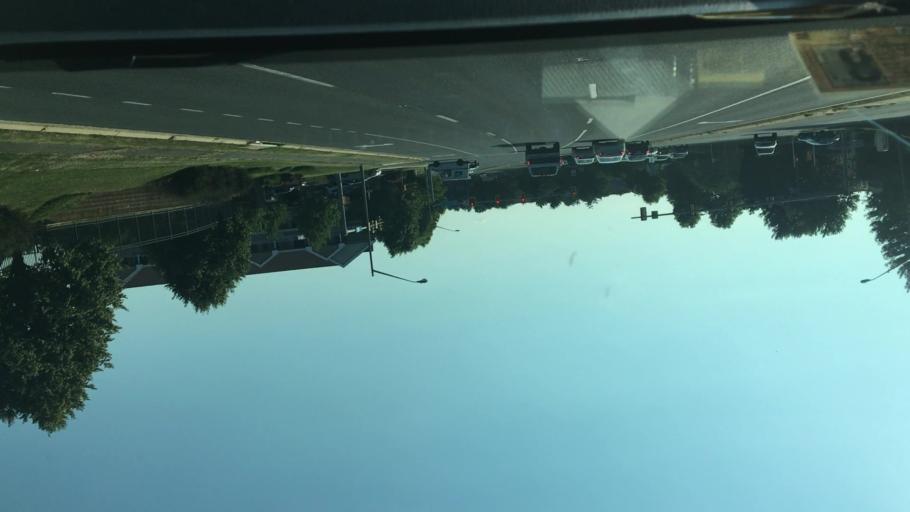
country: US
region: Virginia
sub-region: Prince William County
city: Dale City
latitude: 38.6472
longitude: -77.3129
